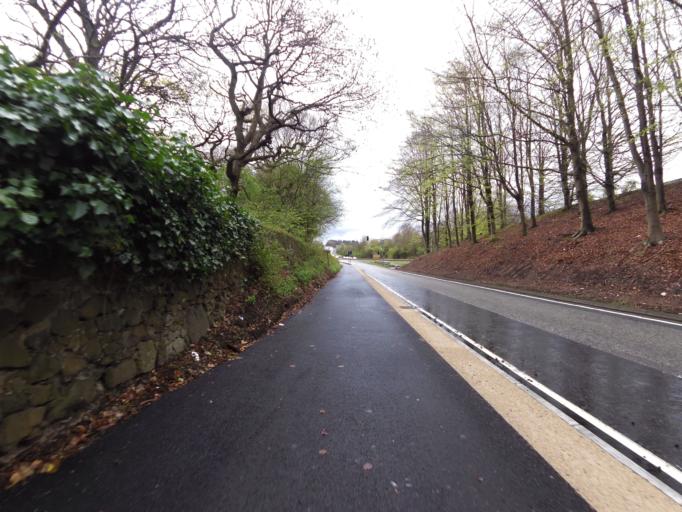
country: GB
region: Scotland
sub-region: Edinburgh
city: Queensferry
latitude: 55.9799
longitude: -3.3472
